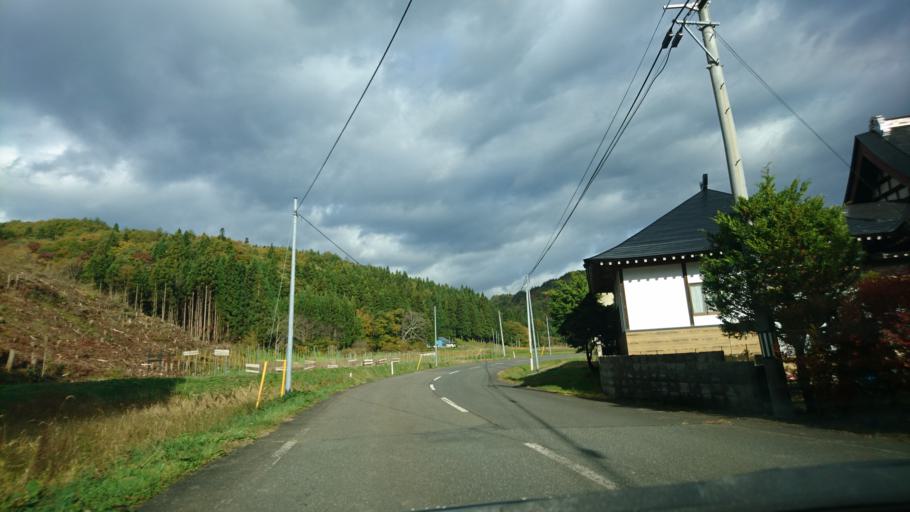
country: JP
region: Iwate
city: Mizusawa
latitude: 39.0947
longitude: 140.9728
